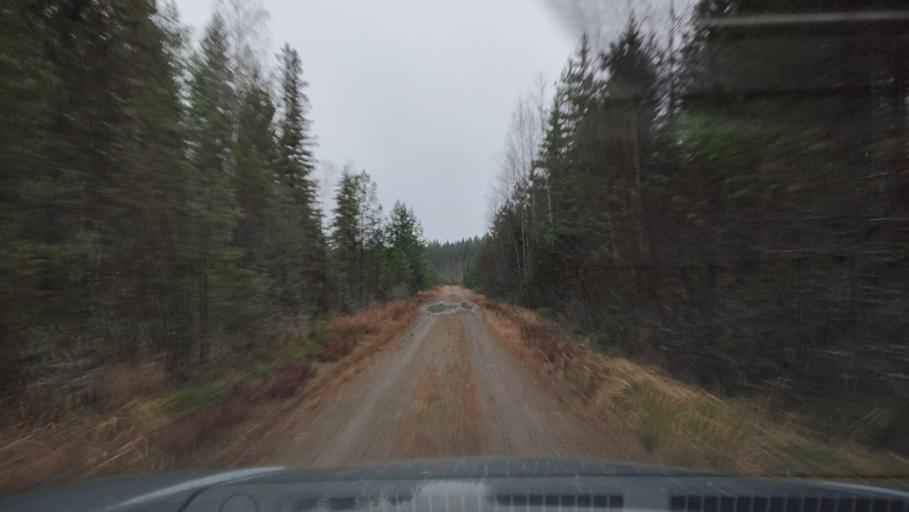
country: FI
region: Southern Ostrobothnia
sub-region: Suupohja
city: Karijoki
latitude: 62.1517
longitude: 21.5903
